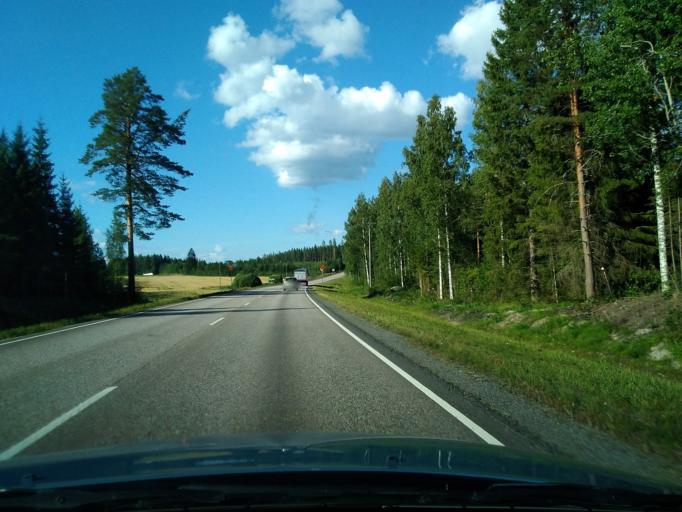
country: FI
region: Central Finland
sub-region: Keuruu
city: Keuruu
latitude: 62.1293
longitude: 24.7361
